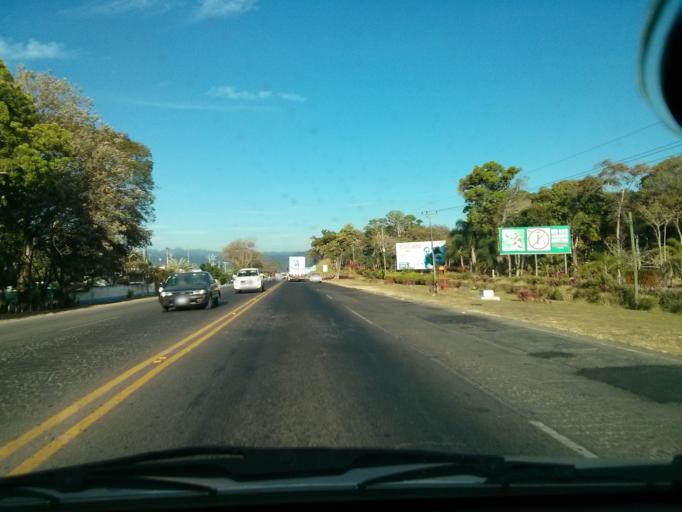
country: CR
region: Alajuela
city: Carrillos
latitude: 10.0035
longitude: -84.2890
